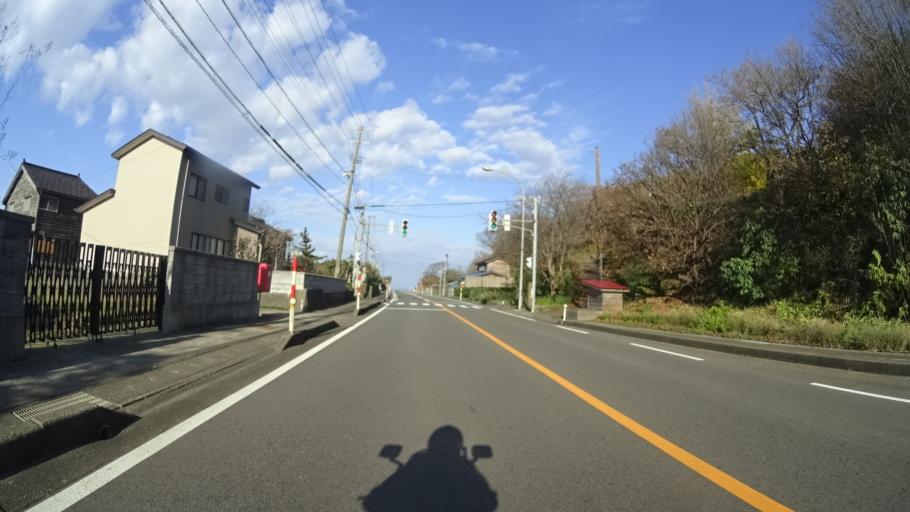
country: JP
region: Niigata
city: Kashiwazaki
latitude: 37.2948
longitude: 138.4061
